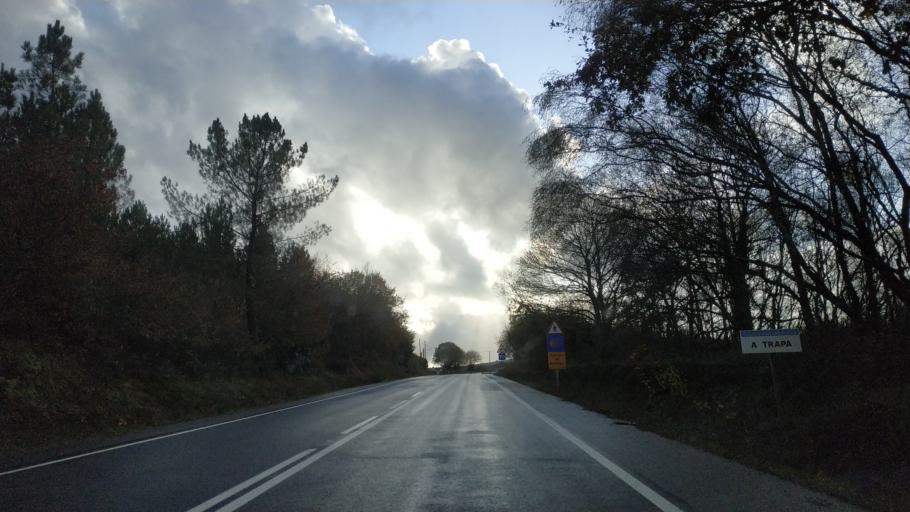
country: ES
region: Galicia
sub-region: Provincia da Coruna
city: Arzua
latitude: 42.9612
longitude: -8.1486
